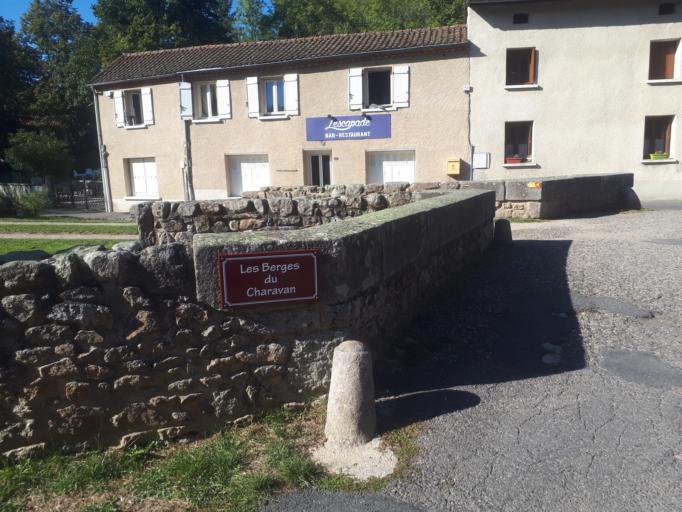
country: FR
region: Rhone-Alpes
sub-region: Departement de la Loire
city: Montbrison
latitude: 45.5892
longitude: 4.0419
